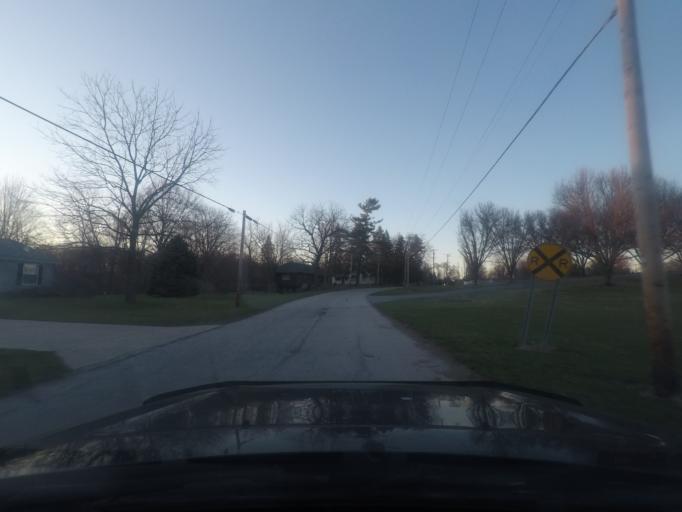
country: US
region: Indiana
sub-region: LaPorte County
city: Kingsford Heights
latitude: 41.5200
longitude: -86.7019
